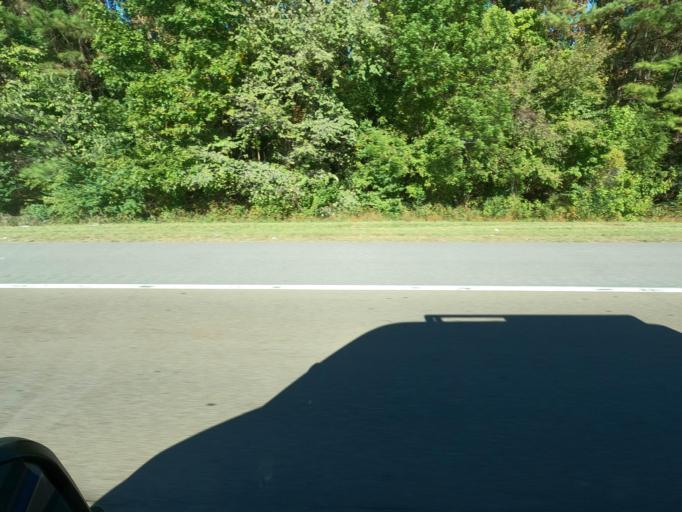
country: US
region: Tennessee
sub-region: Tipton County
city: Munford
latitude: 35.4238
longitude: -89.8155
